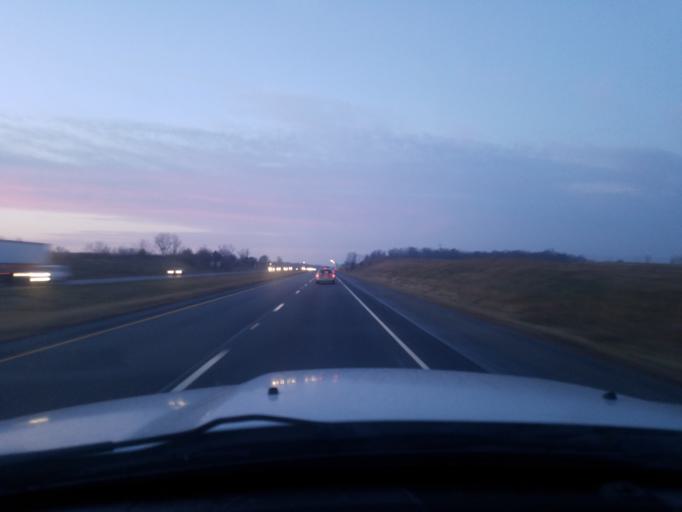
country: US
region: Indiana
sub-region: Huntington County
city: Roanoke
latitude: 41.0026
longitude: -85.2624
